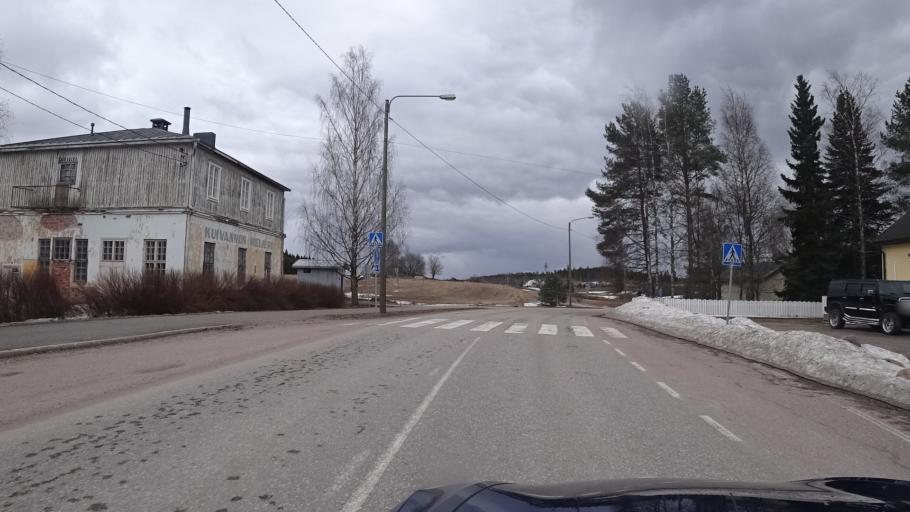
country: FI
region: Paijanne Tavastia
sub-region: Lahti
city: Nastola
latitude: 60.8703
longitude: 26.0118
